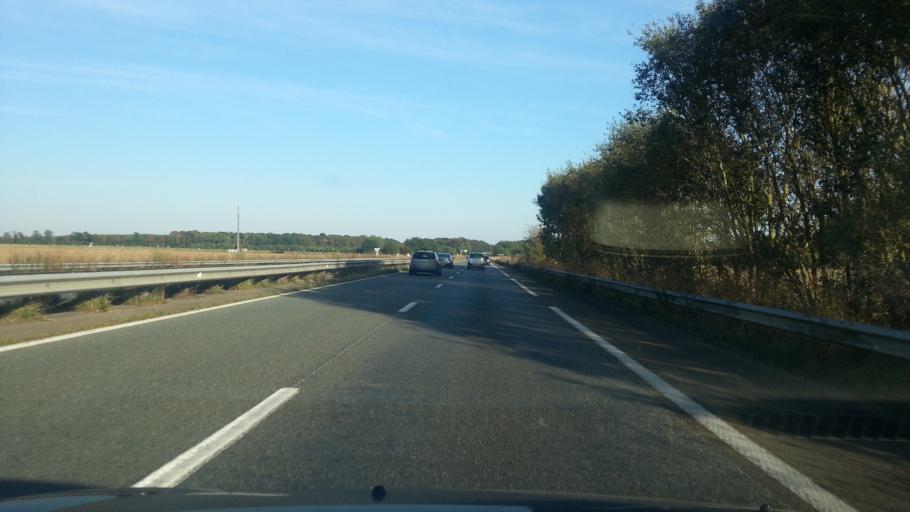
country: FR
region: Picardie
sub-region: Departement de l'Oise
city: Agnetz
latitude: 49.4105
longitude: 2.3331
